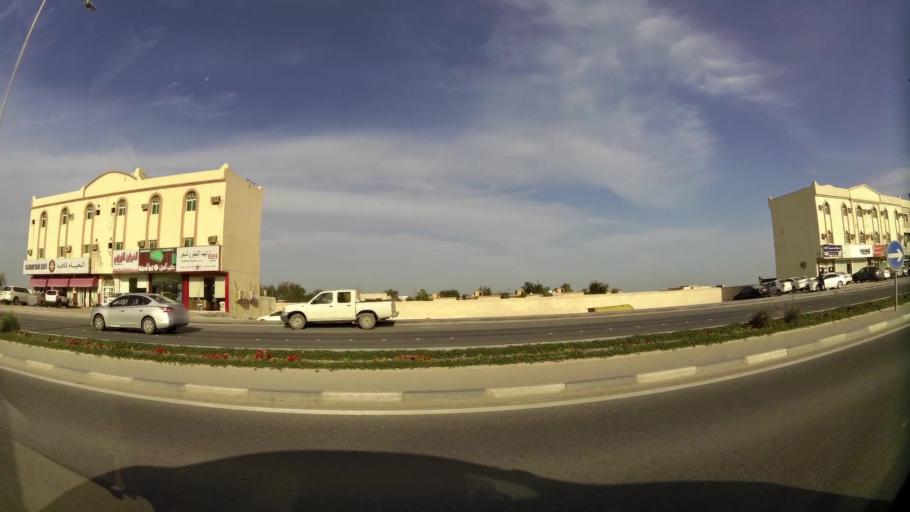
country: QA
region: Al Wakrah
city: Al Wakrah
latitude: 25.1648
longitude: 51.6077
